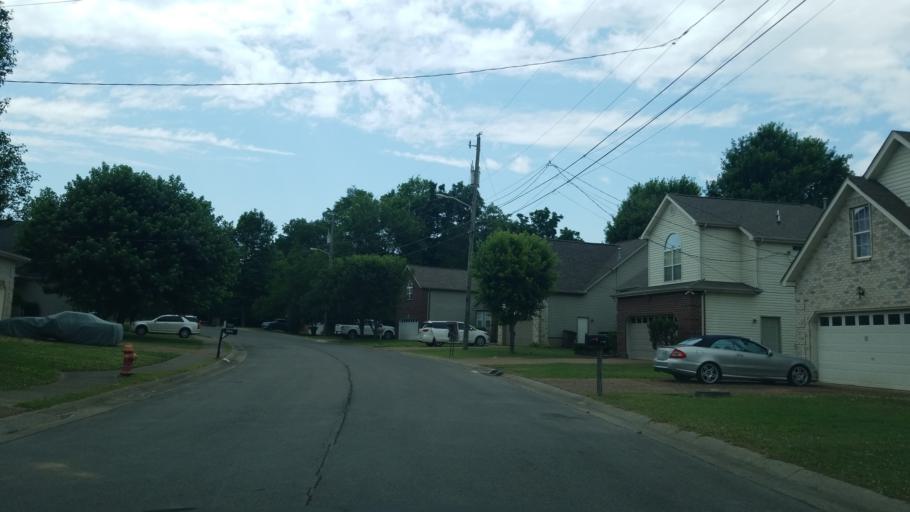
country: US
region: Tennessee
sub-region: Rutherford County
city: La Vergne
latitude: 36.0842
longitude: -86.5829
